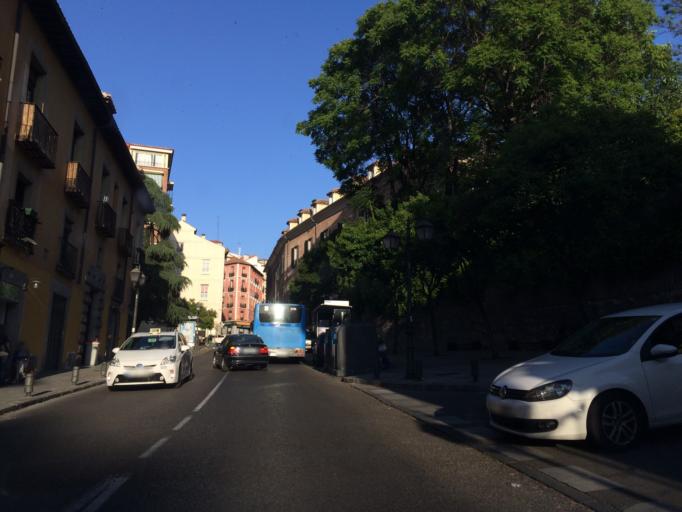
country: ES
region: Madrid
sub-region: Provincia de Madrid
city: Madrid
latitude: 40.4138
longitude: -3.7118
